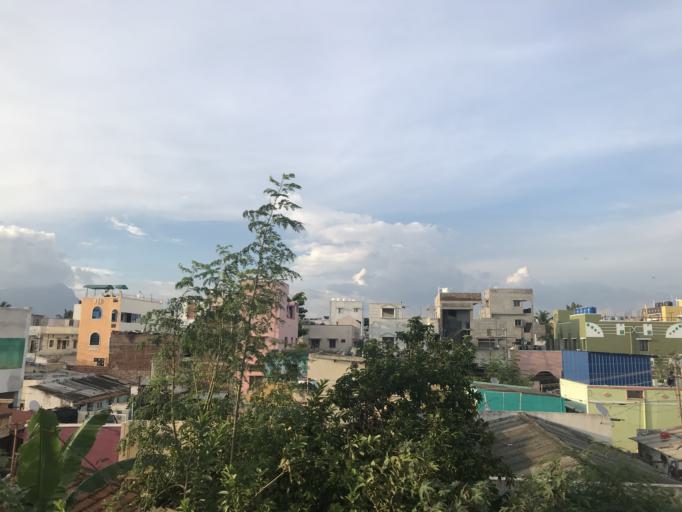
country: IN
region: Tamil Nadu
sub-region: Coimbatore
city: Coimbatore
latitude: 11.0314
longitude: 76.9585
